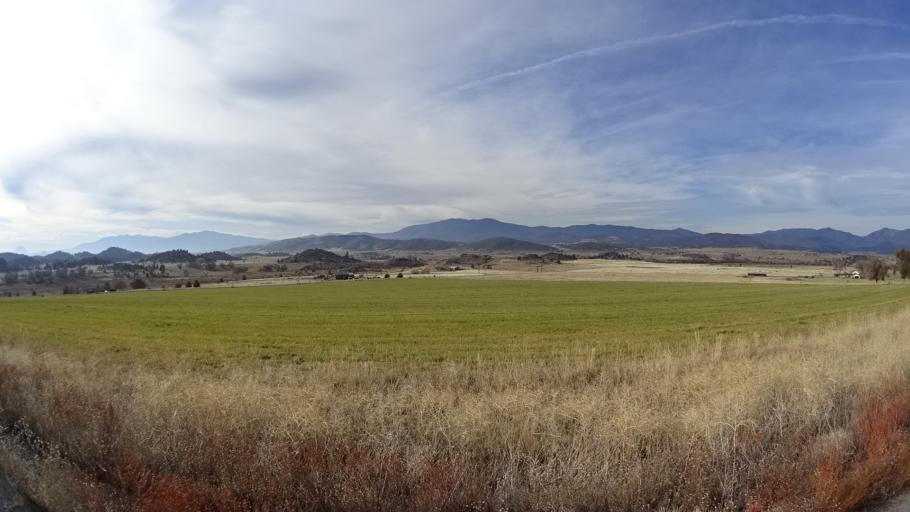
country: US
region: California
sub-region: Siskiyou County
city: Montague
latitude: 41.7086
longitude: -122.5176
